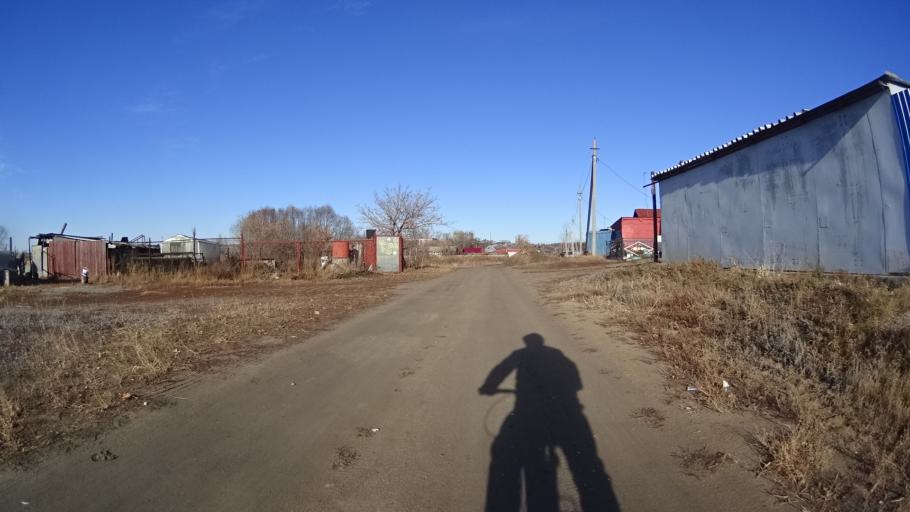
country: RU
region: Chelyabinsk
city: Troitsk
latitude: 54.0881
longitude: 61.5911
